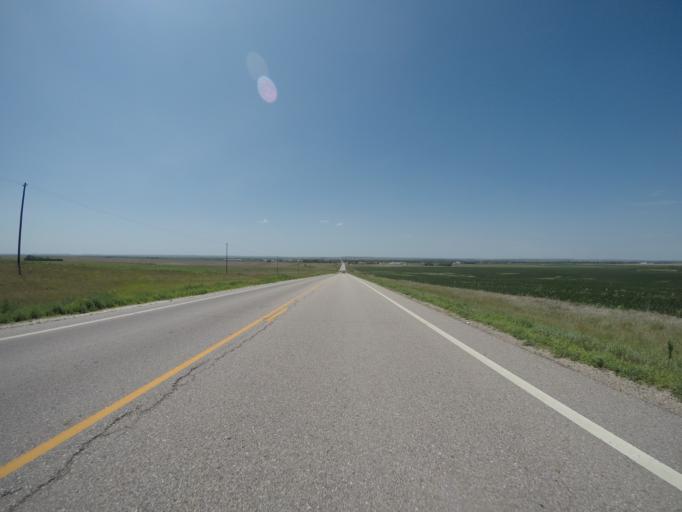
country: US
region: Kansas
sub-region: Osborne County
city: Osborne
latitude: 39.4663
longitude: -98.6945
